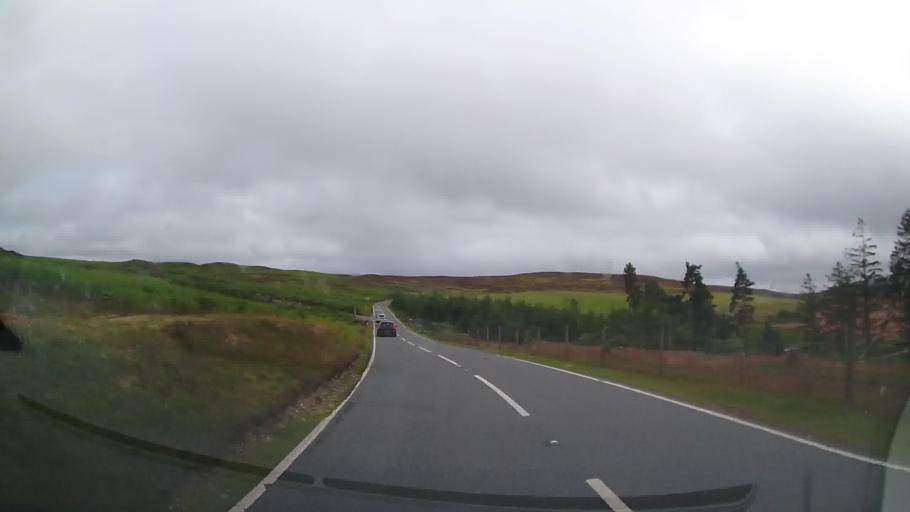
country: GB
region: Wales
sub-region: Denbighshire
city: Llandrillo
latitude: 52.8961
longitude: -3.4916
